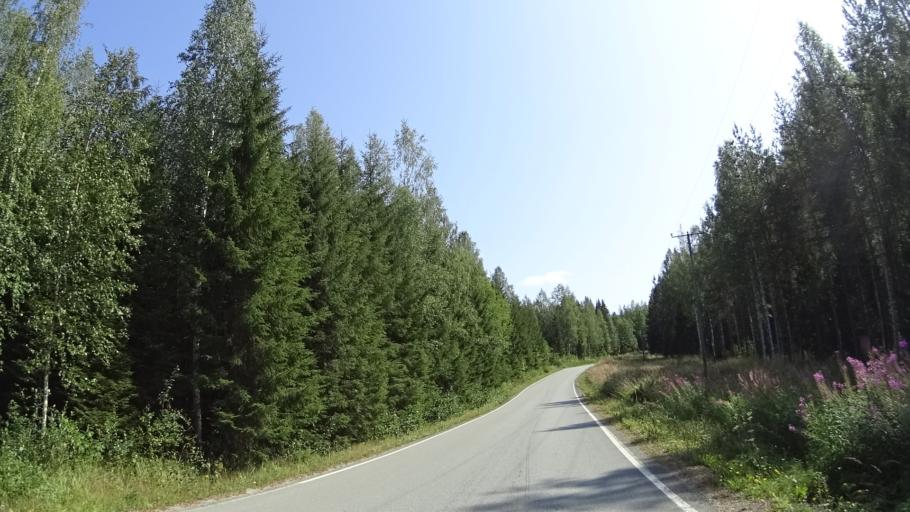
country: FI
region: Central Finland
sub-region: Jaemsae
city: Jaemsae
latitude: 61.7749
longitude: 24.8938
